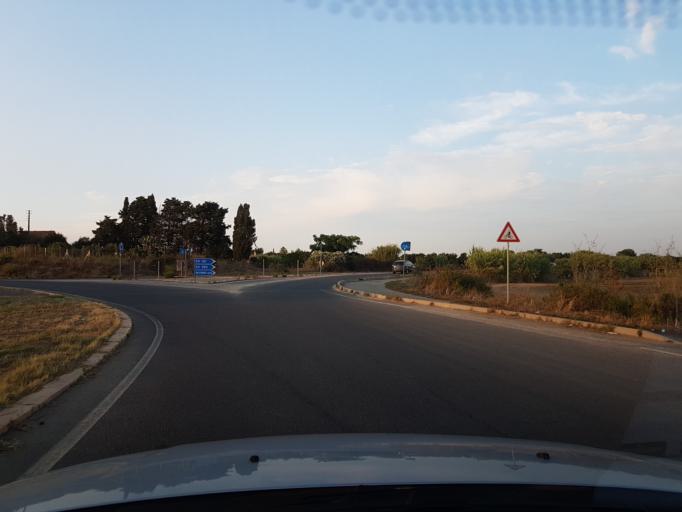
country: IT
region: Sardinia
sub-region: Provincia di Oristano
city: Cabras
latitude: 39.9141
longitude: 8.5427
